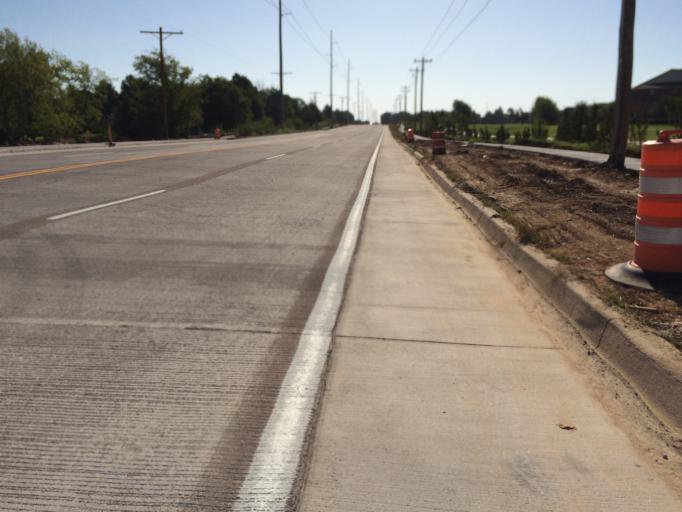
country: US
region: Oklahoma
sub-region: Cleveland County
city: Noble
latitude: 35.1752
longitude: -97.4038
